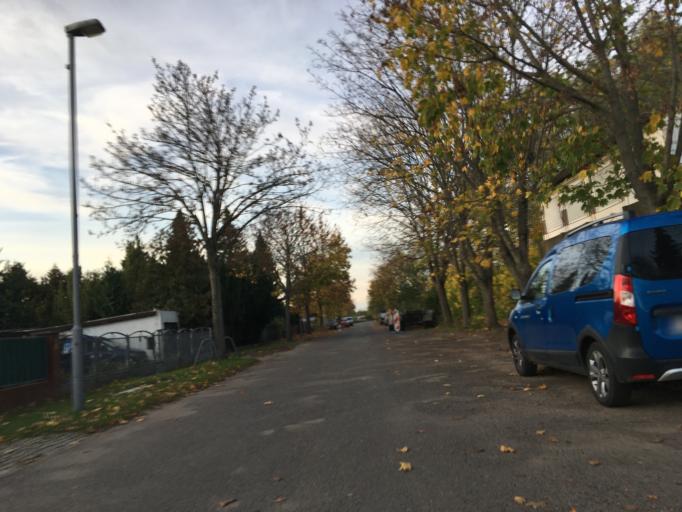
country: DE
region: Berlin
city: Buchholz
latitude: 52.6150
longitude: 13.4364
